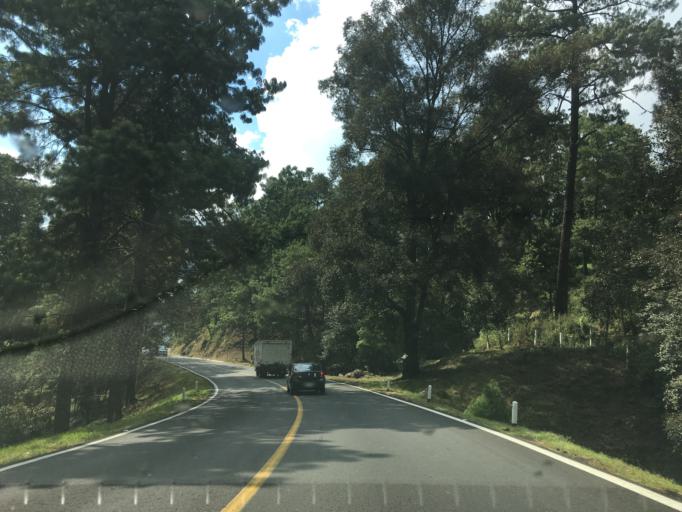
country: MX
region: Michoacan
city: Tingambato
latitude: 19.4917
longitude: -101.8165
